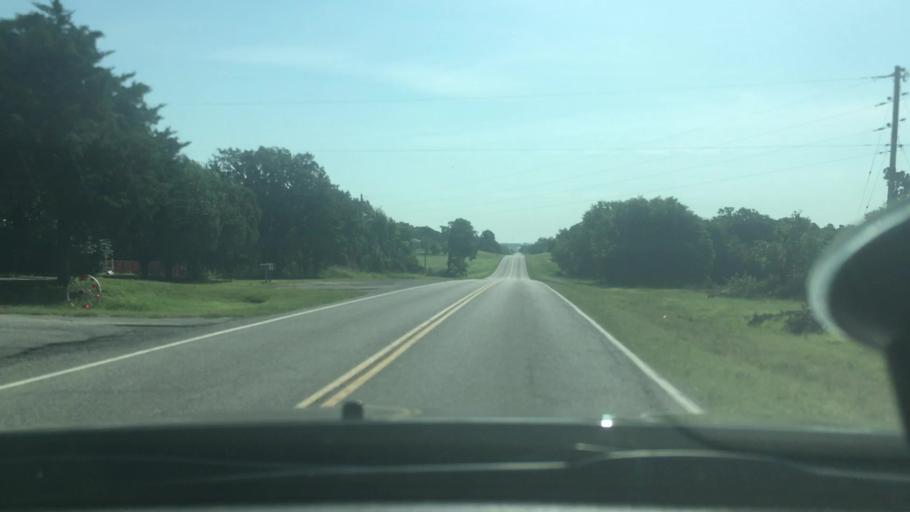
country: US
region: Oklahoma
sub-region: Garvin County
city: Pauls Valley
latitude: 34.6520
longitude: -97.3465
